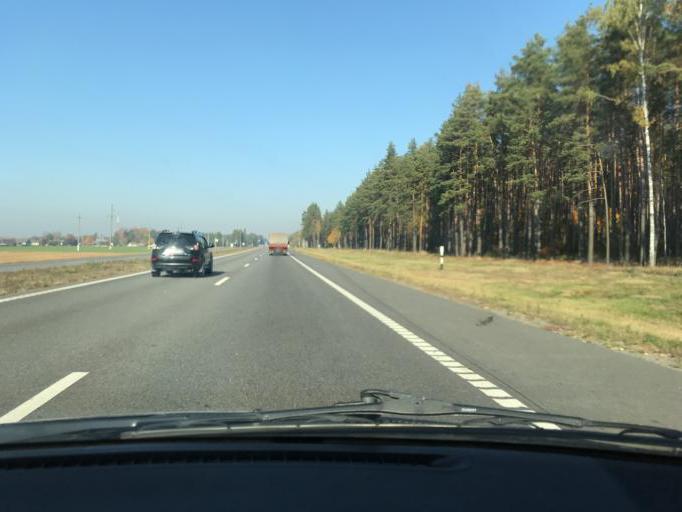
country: BY
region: Minsk
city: Slutsk
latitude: 53.3201
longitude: 27.5350
